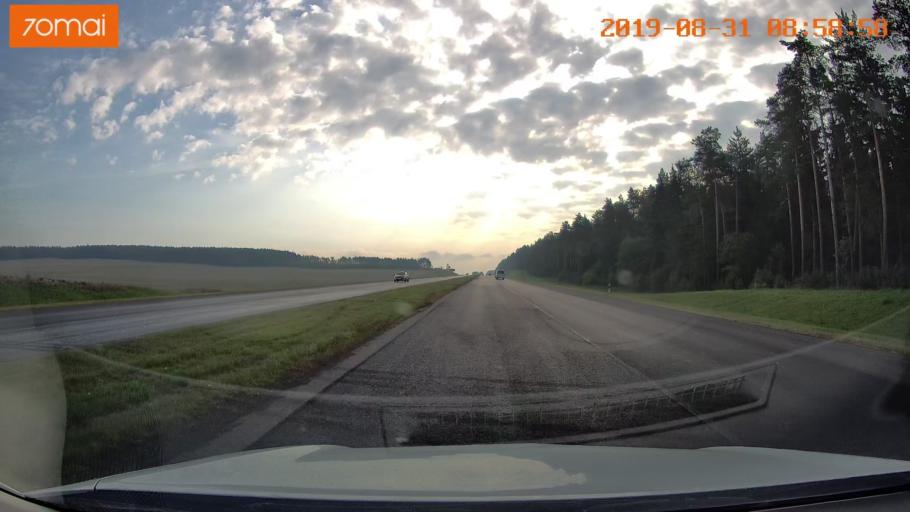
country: BY
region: Minsk
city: Smilavichy
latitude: 53.7651
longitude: 28.1976
